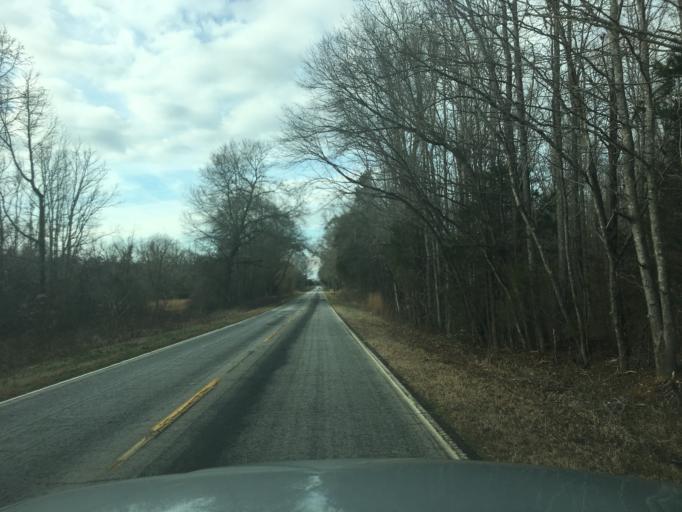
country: US
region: South Carolina
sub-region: Abbeville County
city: Due West
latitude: 34.3496
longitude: -82.5003
